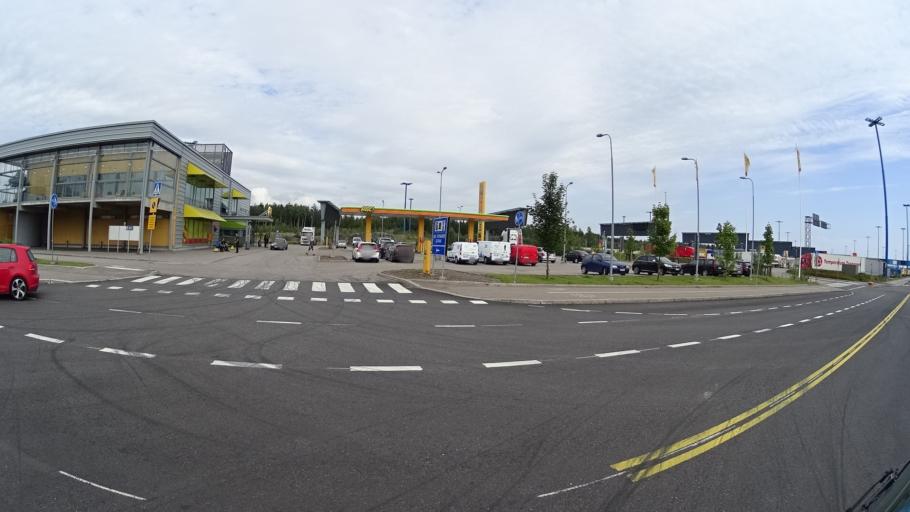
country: FI
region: Uusimaa
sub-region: Helsinki
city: Vantaa
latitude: 60.2247
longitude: 25.1681
